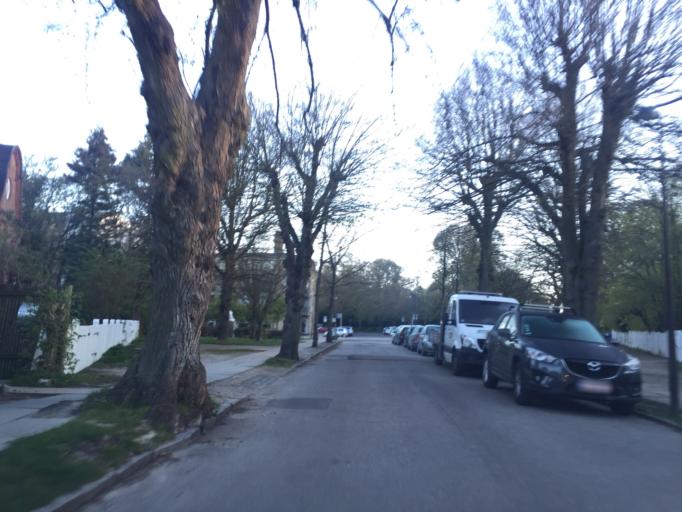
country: DK
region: Capital Region
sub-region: Frederiksberg Kommune
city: Frederiksberg
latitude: 55.6657
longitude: 12.5235
